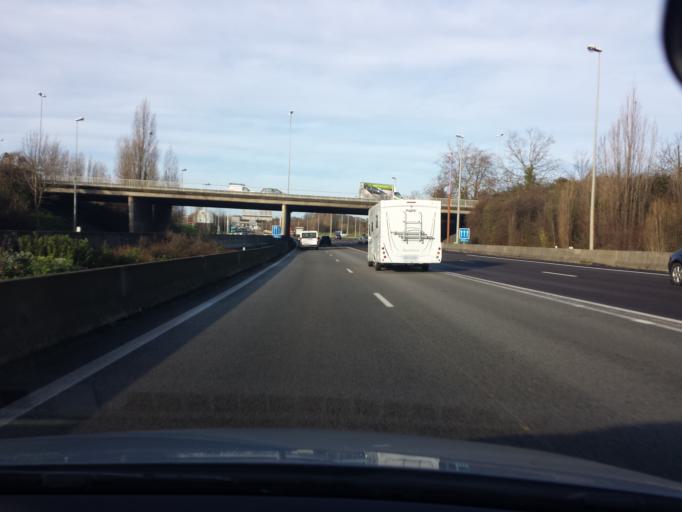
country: FR
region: Ile-de-France
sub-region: Departement des Yvelines
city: Villennes-sur-Seine
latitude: 48.9252
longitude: 1.9986
